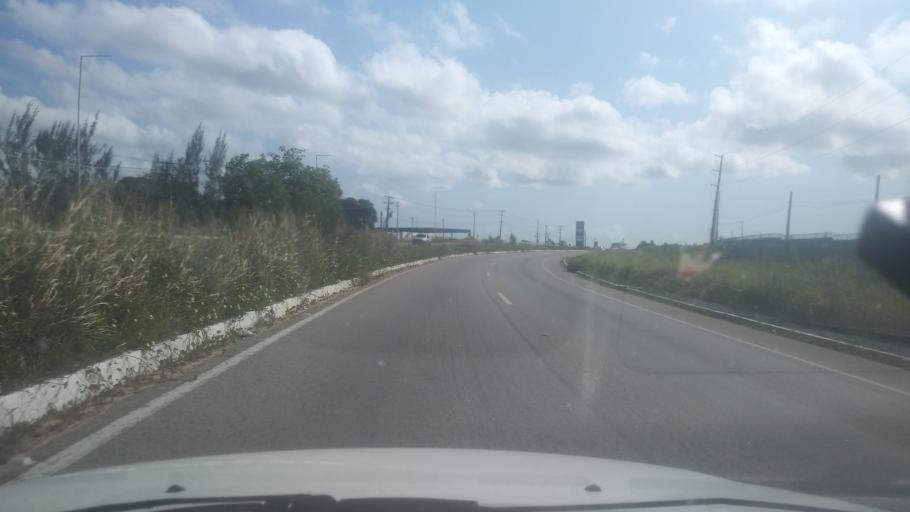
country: BR
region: Rio Grande do Norte
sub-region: Extremoz
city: Extremoz
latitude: -5.7311
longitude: -35.2912
